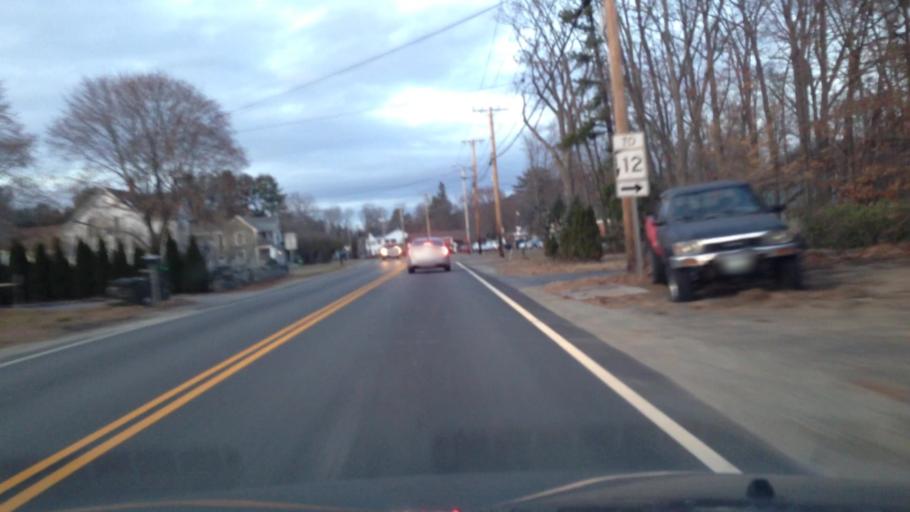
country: US
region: New Hampshire
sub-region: Cheshire County
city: Keene
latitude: 42.9041
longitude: -72.2650
